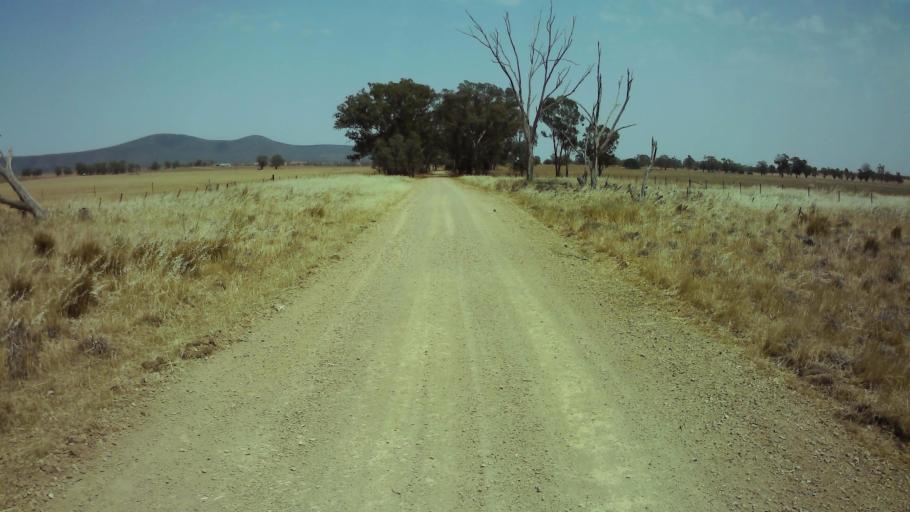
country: AU
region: New South Wales
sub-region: Weddin
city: Grenfell
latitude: -33.8846
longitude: 148.0810
